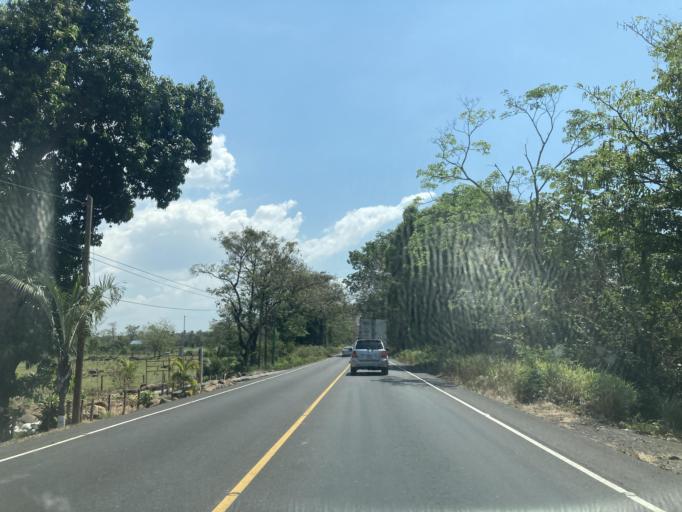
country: GT
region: Santa Rosa
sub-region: Municipio de Taxisco
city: Taxisco
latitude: 14.0939
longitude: -90.5706
